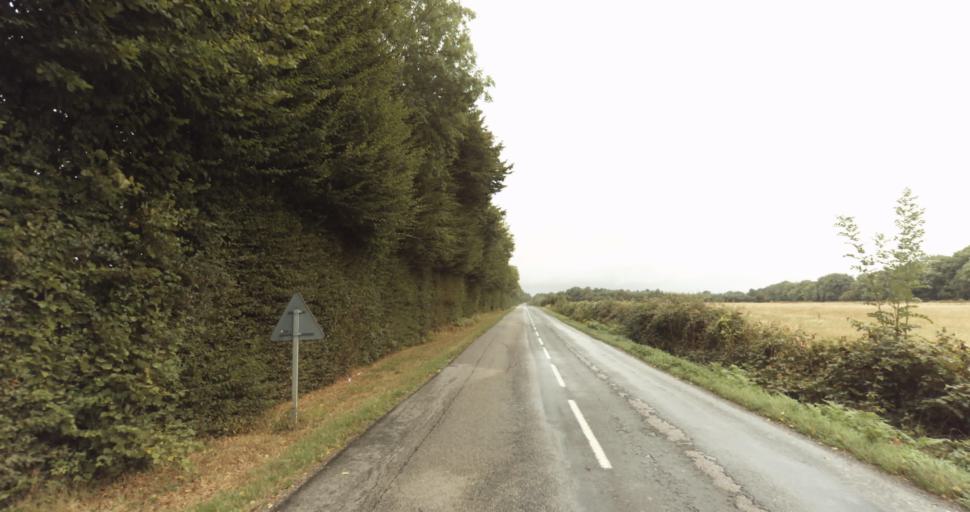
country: FR
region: Lower Normandy
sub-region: Departement de l'Orne
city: Vimoutiers
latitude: 48.8686
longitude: 0.1849
